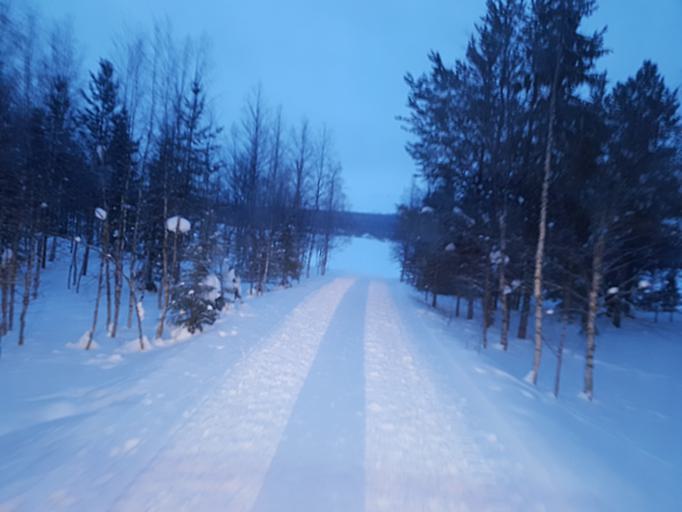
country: FI
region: Lapland
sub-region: Tunturi-Lappi
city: Kolari
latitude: 67.6126
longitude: 24.1474
